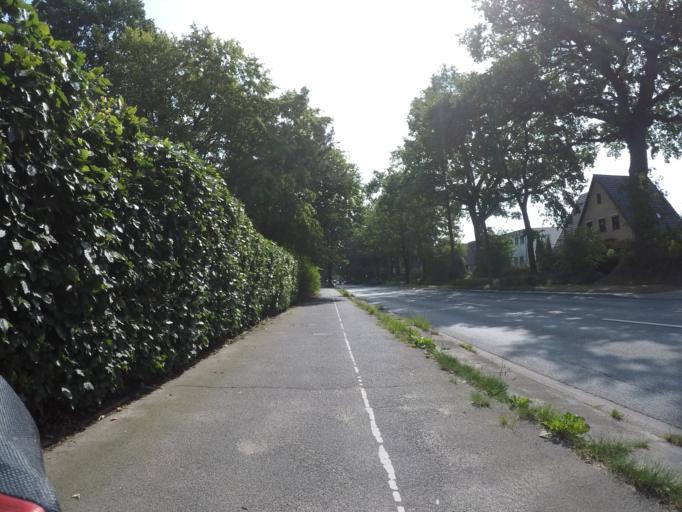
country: DE
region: Hamburg
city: Poppenbuettel
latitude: 53.6658
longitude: 10.0715
